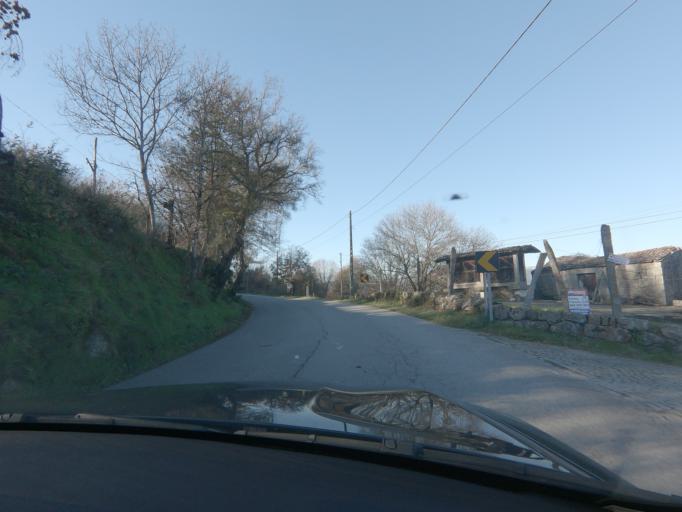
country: PT
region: Viseu
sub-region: Oliveira de Frades
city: Oliveira de Frades
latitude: 40.7297
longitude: -8.1543
